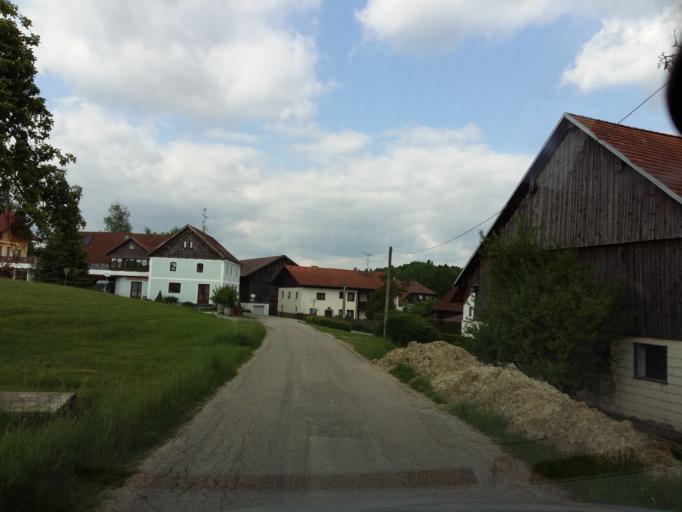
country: AT
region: Upper Austria
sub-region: Politischer Bezirk Scharding
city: Sankt Marienkirchen bei Schaerding
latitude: 48.3837
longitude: 13.4911
